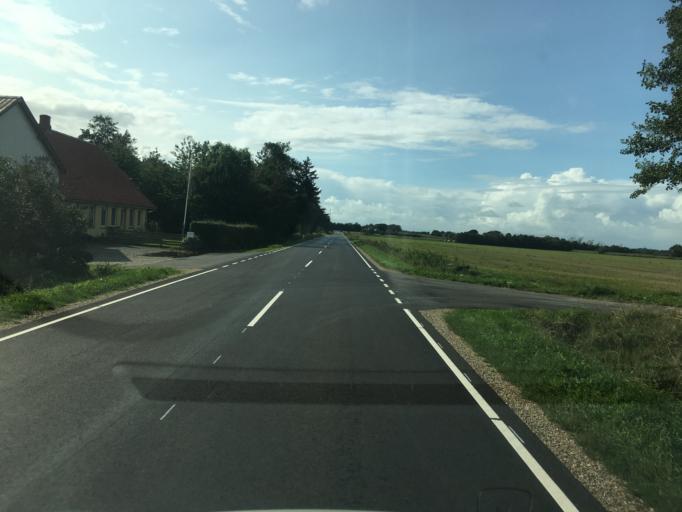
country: DK
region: South Denmark
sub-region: Tonder Kommune
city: Tonder
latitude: 55.0153
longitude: 8.8620
